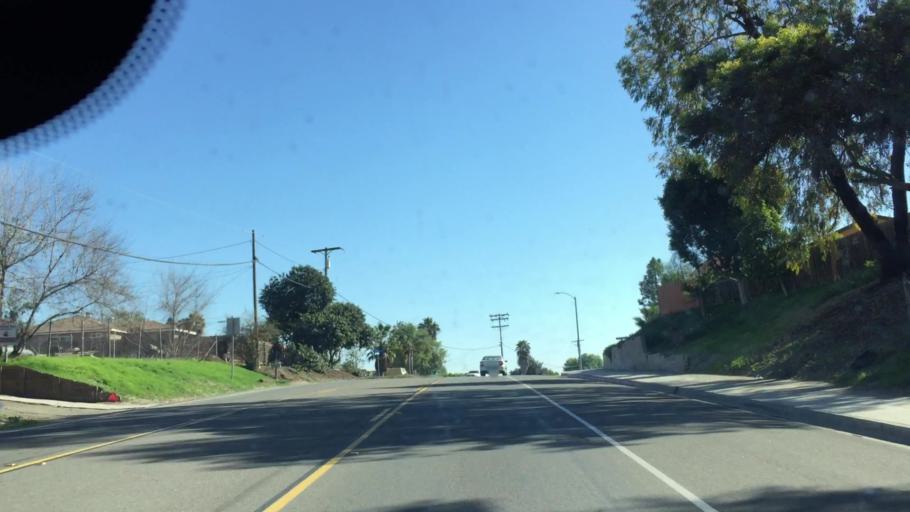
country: US
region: California
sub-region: San Diego County
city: Vista
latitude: 33.2270
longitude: -117.2470
